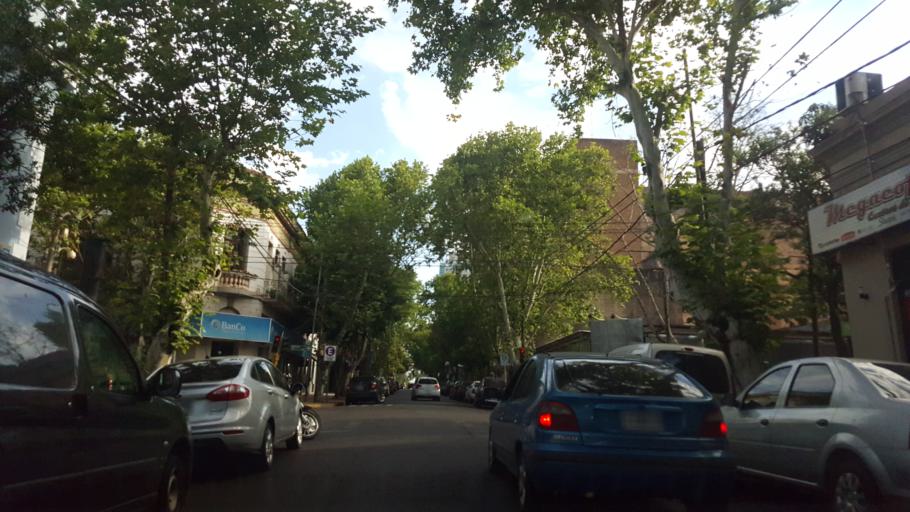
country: AR
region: Misiones
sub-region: Departamento de Capital
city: Posadas
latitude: -27.3639
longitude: -55.8932
